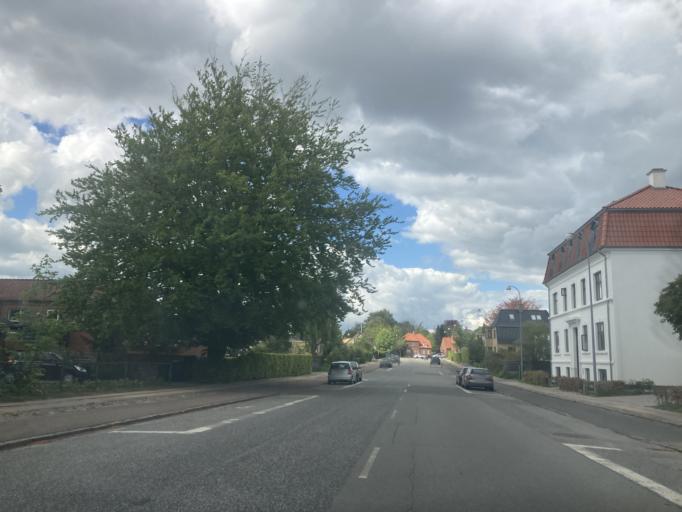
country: DK
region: Capital Region
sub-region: Gladsaxe Municipality
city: Buddinge
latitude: 55.7635
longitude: 12.4849
